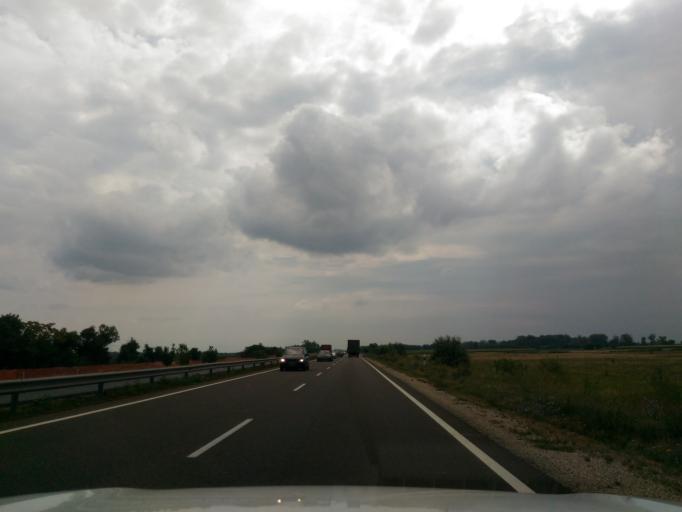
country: HU
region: Pest
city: Cegled
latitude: 47.1906
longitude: 19.8713
